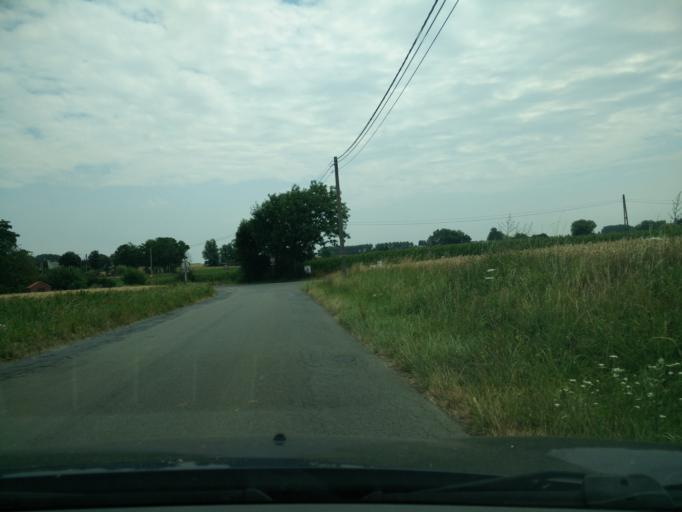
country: BE
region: Wallonia
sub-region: Province du Hainaut
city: Roeulx
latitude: 50.5519
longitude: 4.1139
